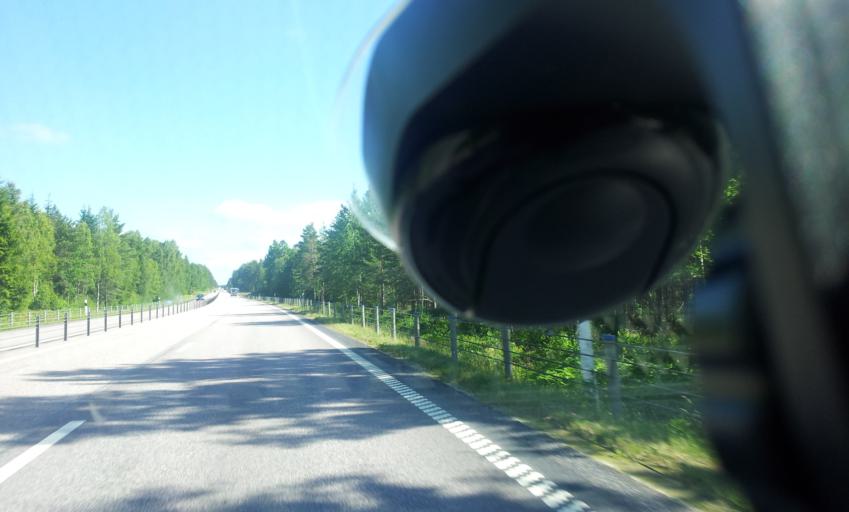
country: SE
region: Kalmar
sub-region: Monsteras Kommun
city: Timmernabben
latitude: 56.9904
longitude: 16.4104
